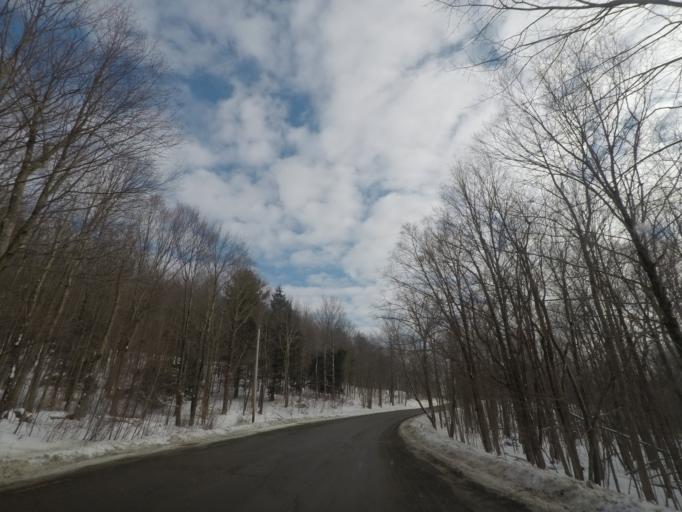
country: US
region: New York
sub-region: Rensselaer County
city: Averill Park
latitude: 42.6226
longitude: -73.4963
